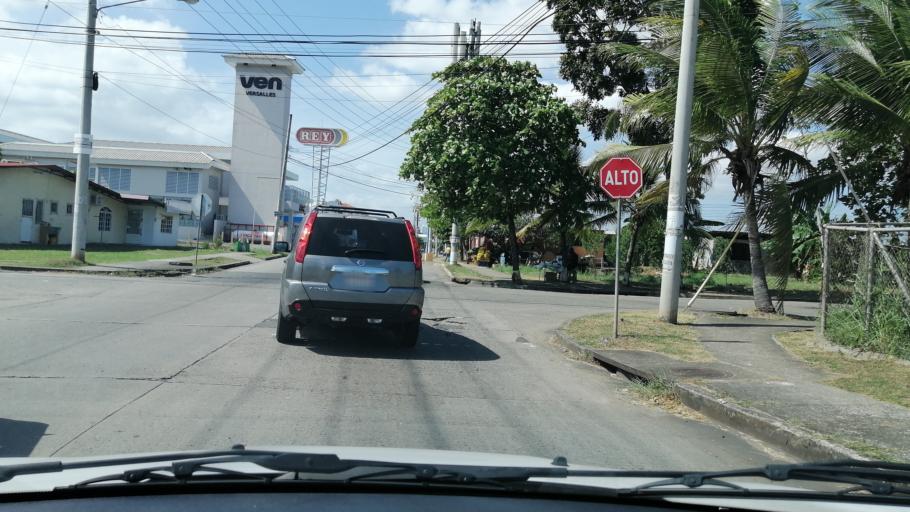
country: PA
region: Panama
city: Tocumen
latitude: 9.0448
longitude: -79.4143
